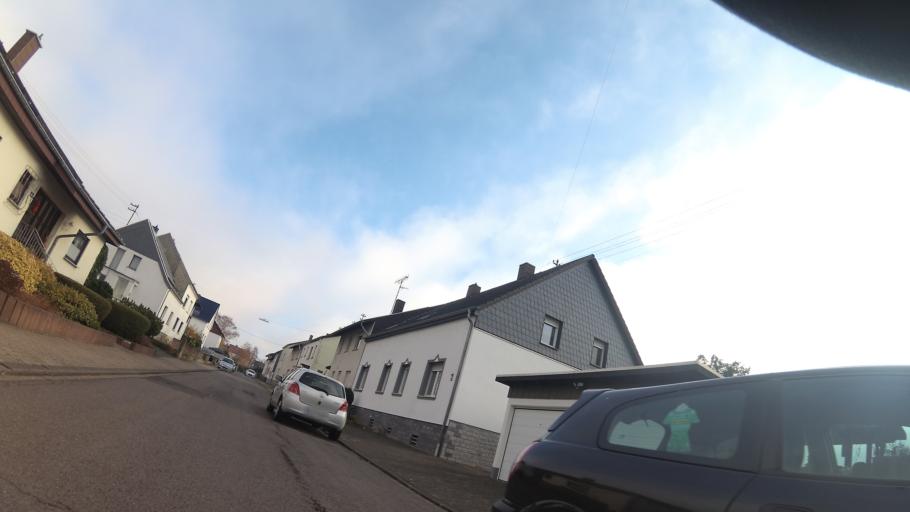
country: DE
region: Saarland
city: Ensdorf
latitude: 49.3041
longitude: 6.7811
